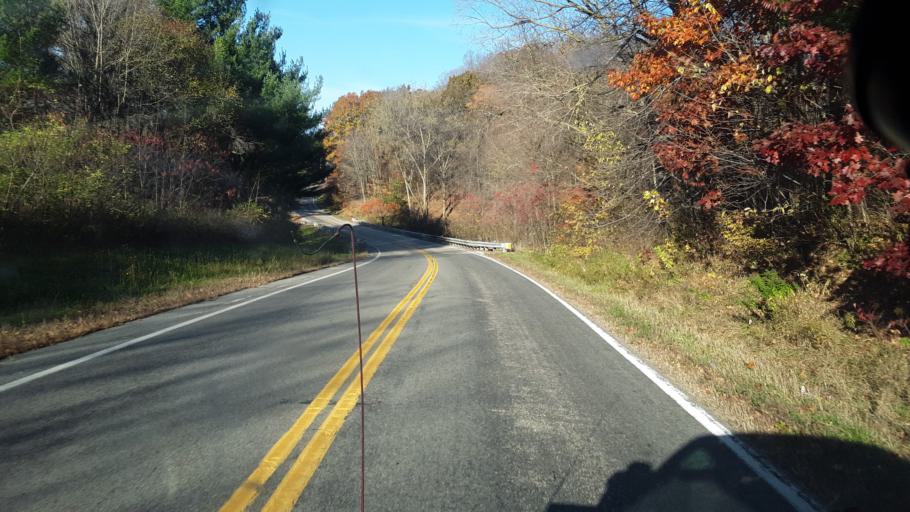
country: US
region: Wisconsin
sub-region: Vernon County
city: Hillsboro
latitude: 43.6607
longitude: -90.4293
